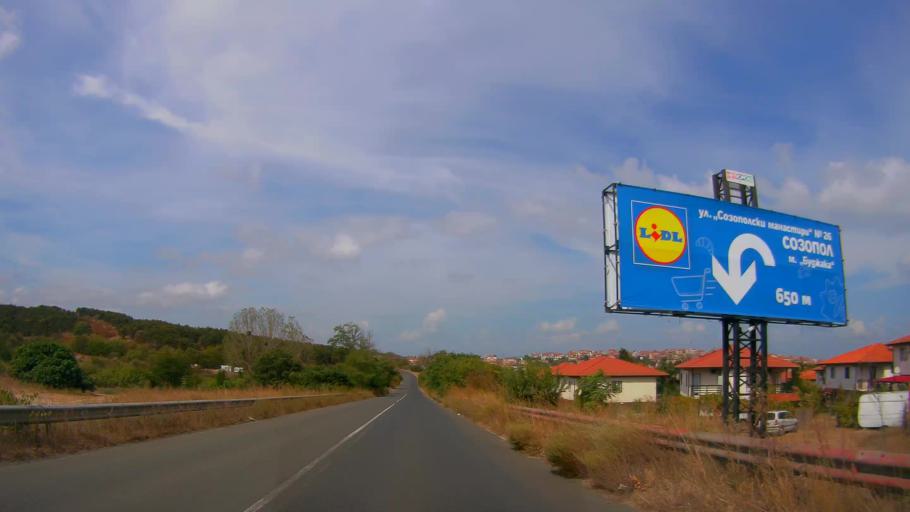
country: BG
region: Burgas
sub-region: Obshtina Sozopol
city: Sozopol
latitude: 42.4081
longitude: 27.6999
